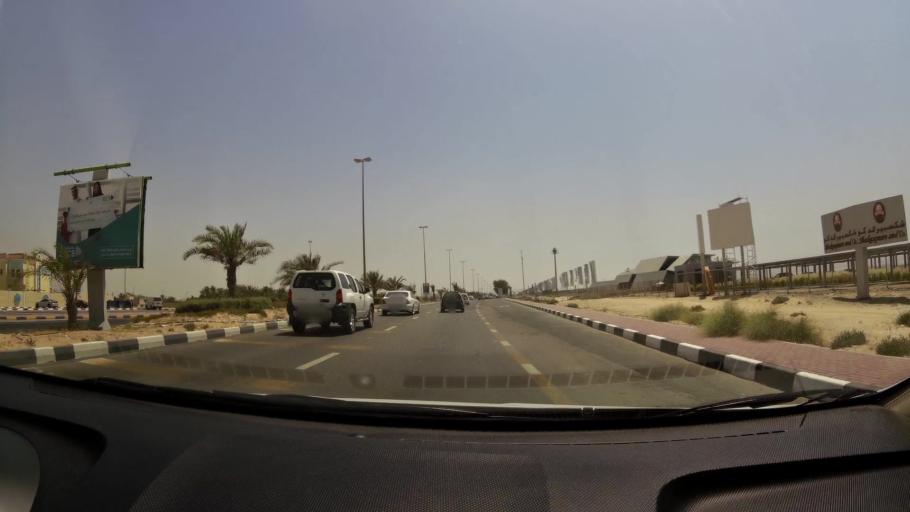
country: AE
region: Ajman
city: Ajman
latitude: 25.4263
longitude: 55.4998
